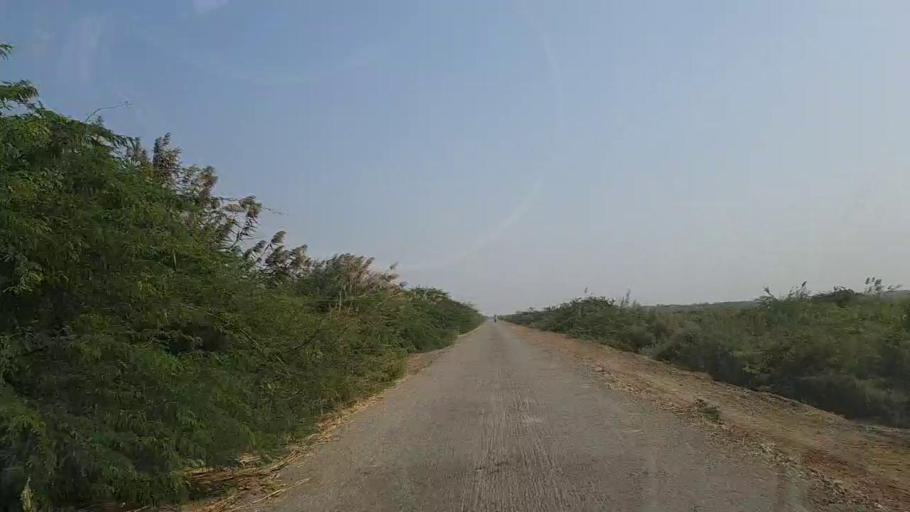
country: PK
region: Sindh
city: Keti Bandar
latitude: 24.2314
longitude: 67.6507
